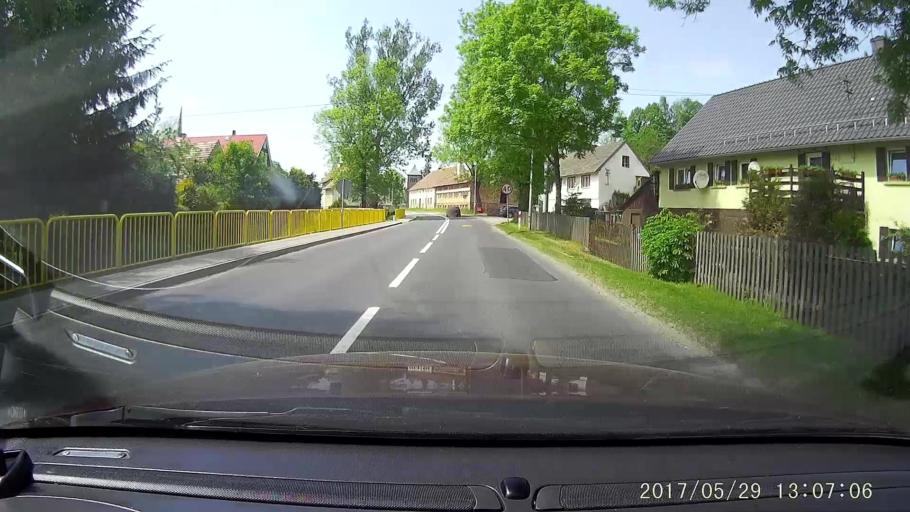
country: PL
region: Lower Silesian Voivodeship
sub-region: Powiat jeleniogorski
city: Stara Kamienica
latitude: 50.9557
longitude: 15.5757
